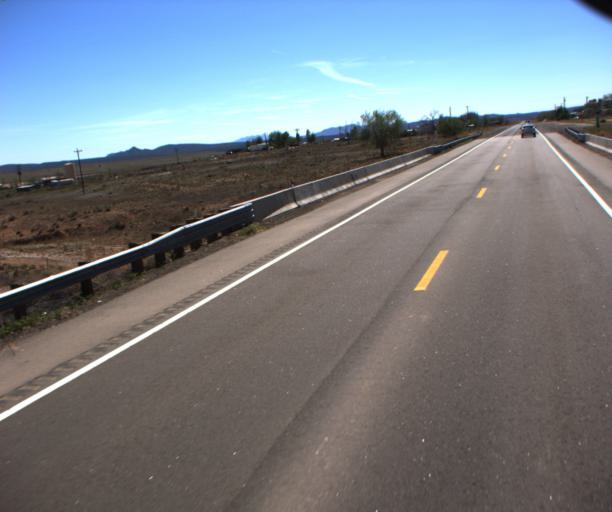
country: US
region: Arizona
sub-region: Mohave County
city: Peach Springs
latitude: 35.4867
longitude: -113.5596
